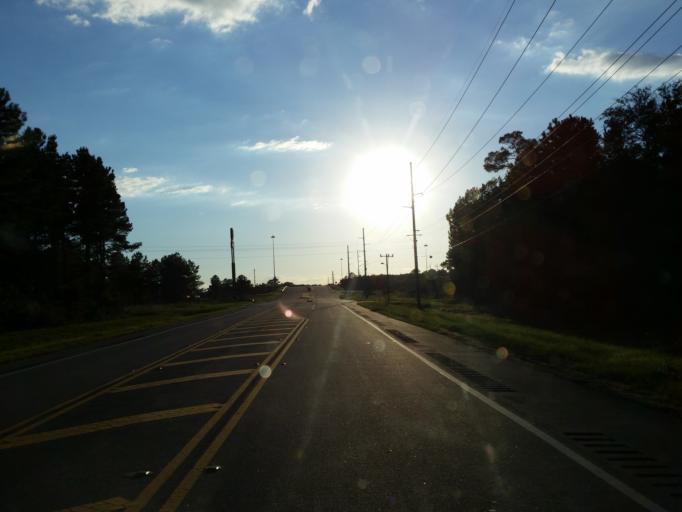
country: US
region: Georgia
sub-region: Crisp County
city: Cordele
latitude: 32.0054
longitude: -83.7534
